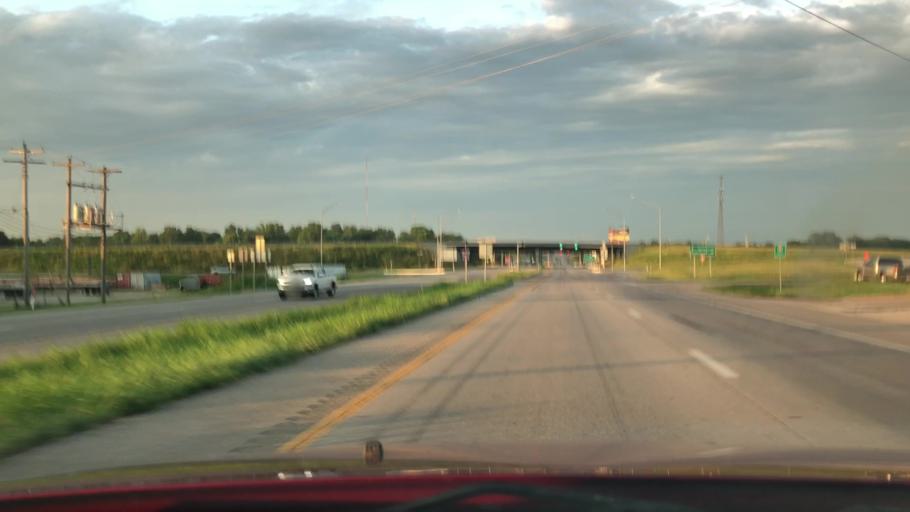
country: US
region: Missouri
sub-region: Greene County
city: Battlefield
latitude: 37.1600
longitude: -93.4018
